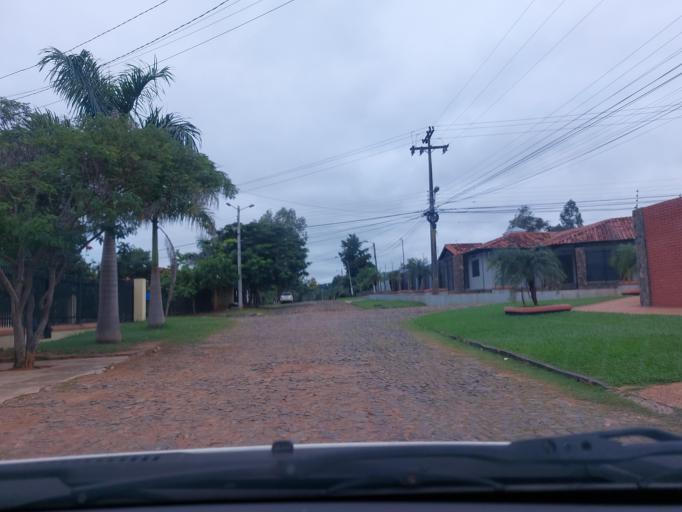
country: PY
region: San Pedro
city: Guayaybi
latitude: -24.6666
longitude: -56.4360
